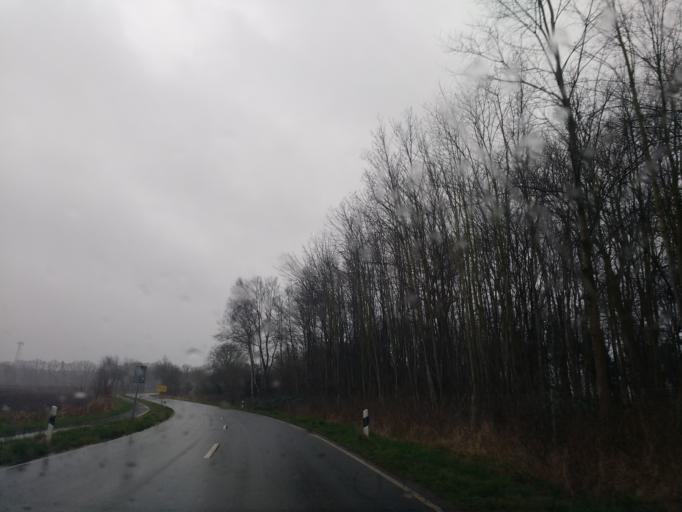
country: DE
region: Schleswig-Holstein
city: Wangels
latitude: 54.3029
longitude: 10.7723
